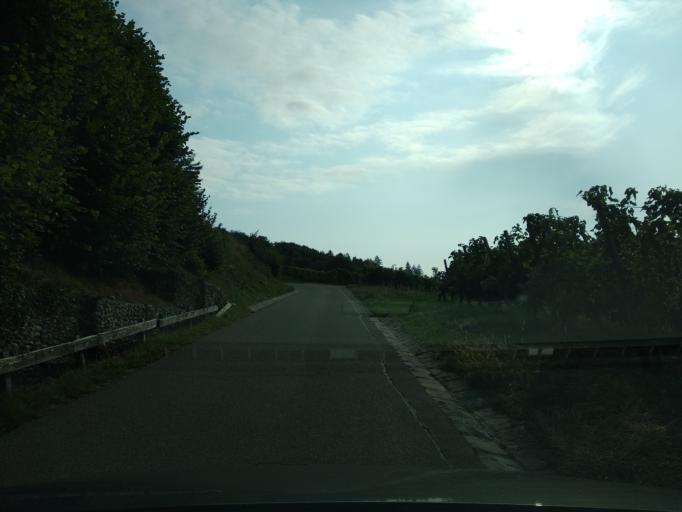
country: CH
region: Zurich
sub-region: Bezirk Andelfingen
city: Marthalen
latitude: 47.6424
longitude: 8.6738
